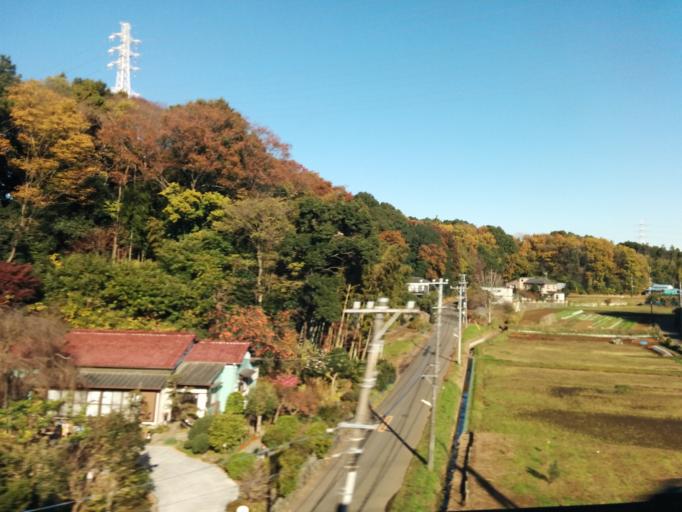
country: JP
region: Kanagawa
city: Atsugi
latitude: 35.4113
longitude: 139.4189
